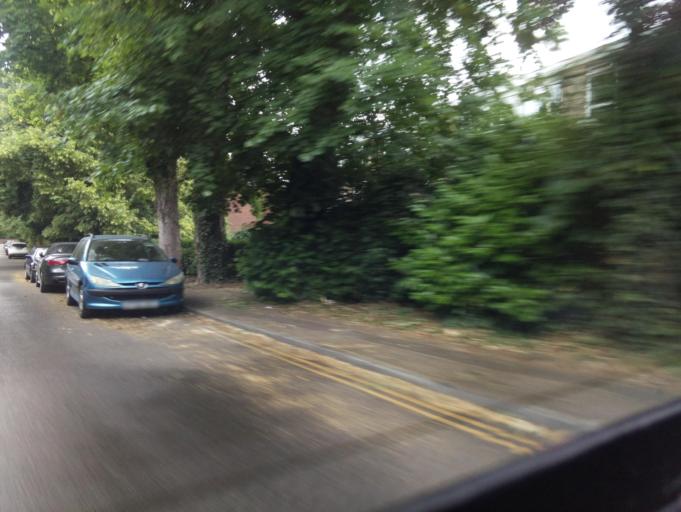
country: GB
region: England
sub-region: Surrey
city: Redhill
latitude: 51.2387
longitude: -0.1856
